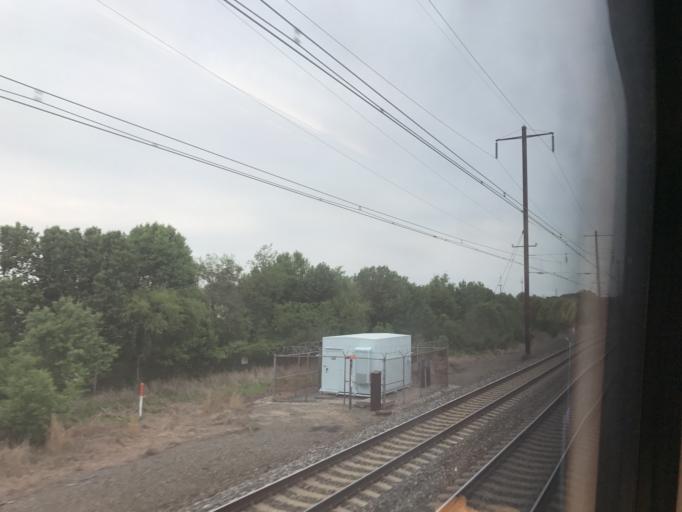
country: US
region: Maryland
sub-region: Anne Arundel County
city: Odenton
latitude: 39.0774
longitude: -76.7147
